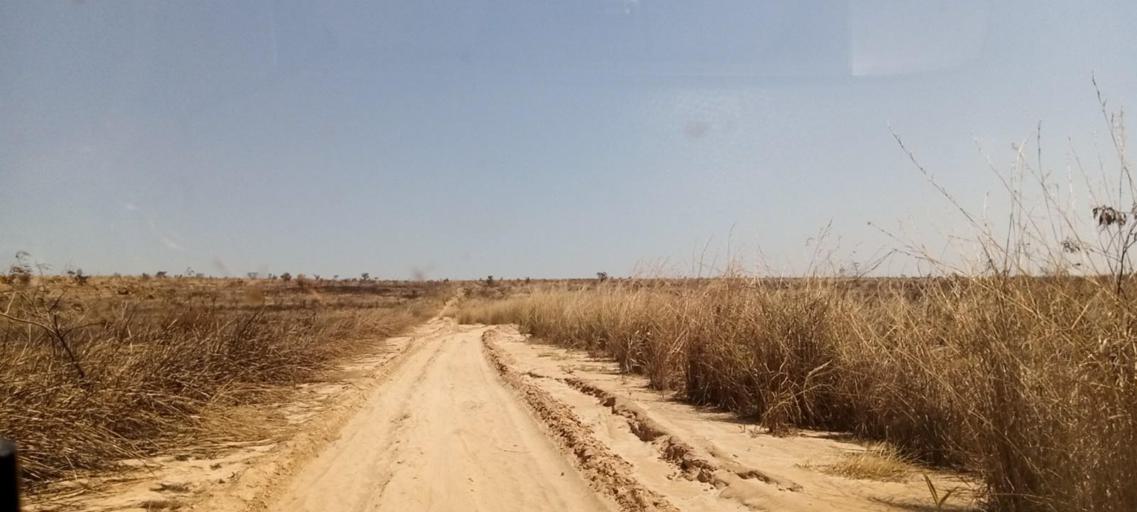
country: CD
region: Kasai-Oriental
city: Kabinda
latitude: -5.9395
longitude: 24.8129
